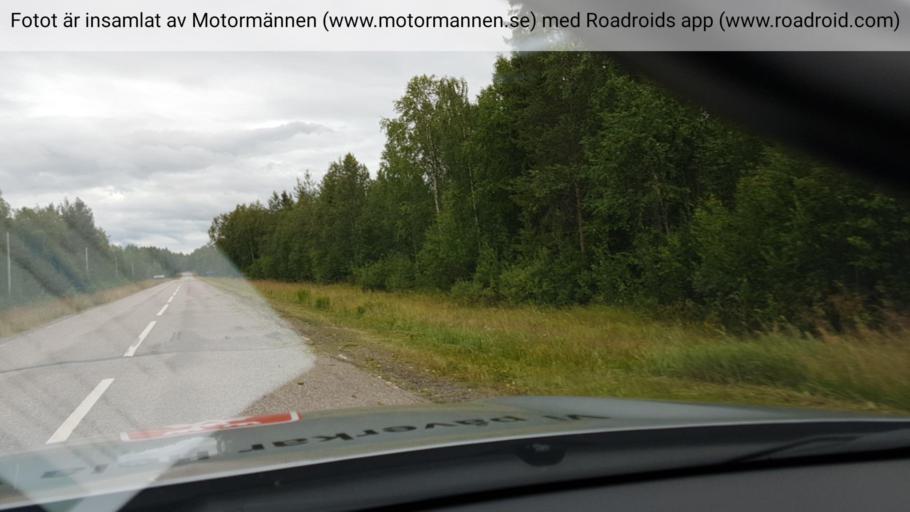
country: SE
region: Norrbotten
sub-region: Overkalix Kommun
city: OEverkalix
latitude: 66.7737
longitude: 22.9013
